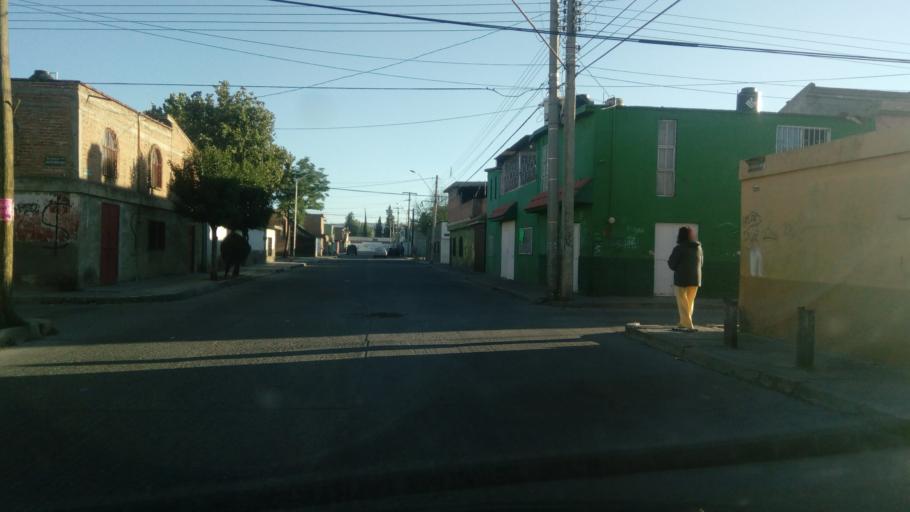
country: MX
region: Durango
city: Victoria de Durango
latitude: 23.9991
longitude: -104.6802
